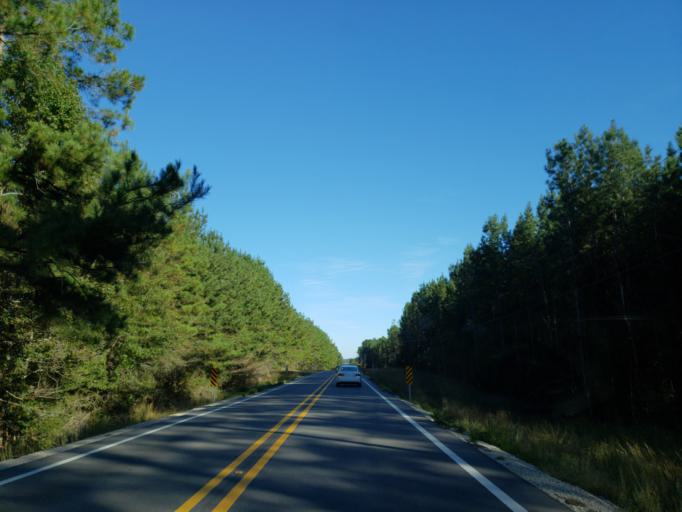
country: US
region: Mississippi
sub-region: Perry County
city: Richton
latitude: 31.3696
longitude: -89.0699
